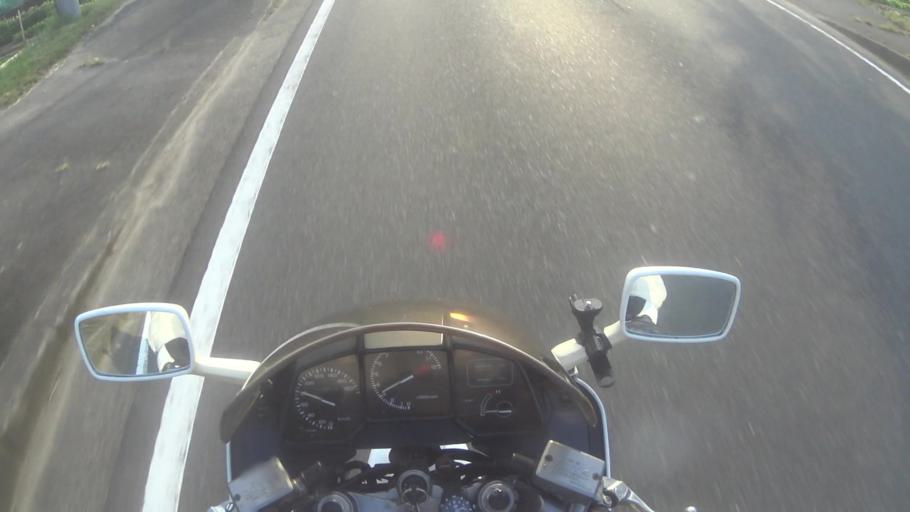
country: JP
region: Kyoto
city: Miyazu
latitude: 35.6039
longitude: 135.0512
